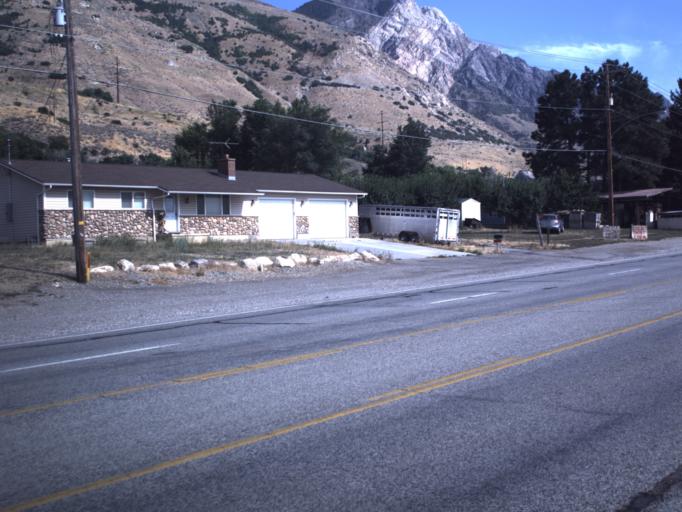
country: US
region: Utah
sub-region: Box Elder County
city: Willard
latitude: 41.4343
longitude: -112.0359
